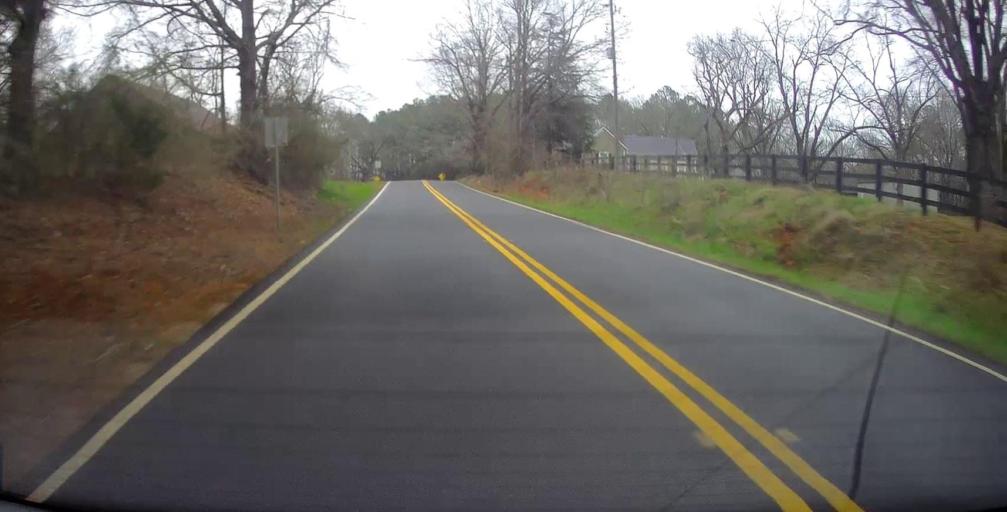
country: US
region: Georgia
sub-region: Lamar County
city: Barnesville
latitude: 33.0627
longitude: -84.2501
